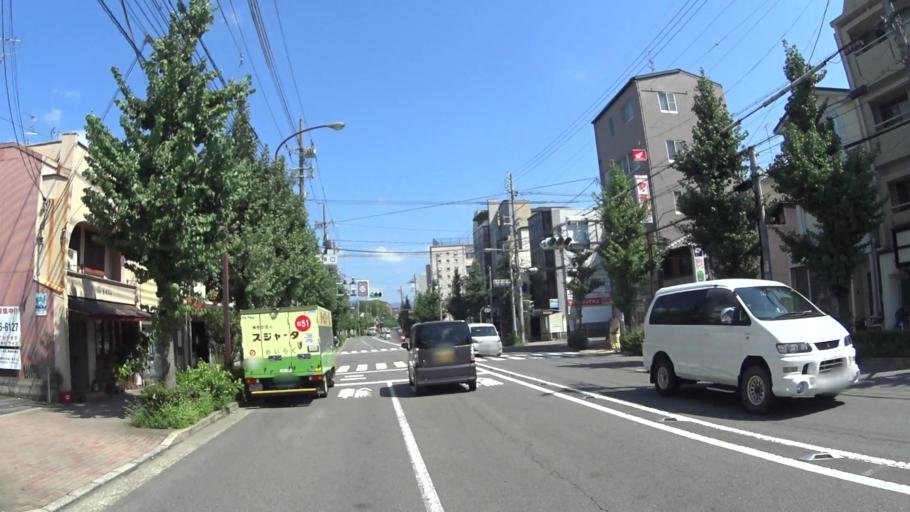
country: JP
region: Kyoto
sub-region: Kyoto-shi
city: Kamigyo-ku
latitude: 35.0209
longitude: 135.7694
